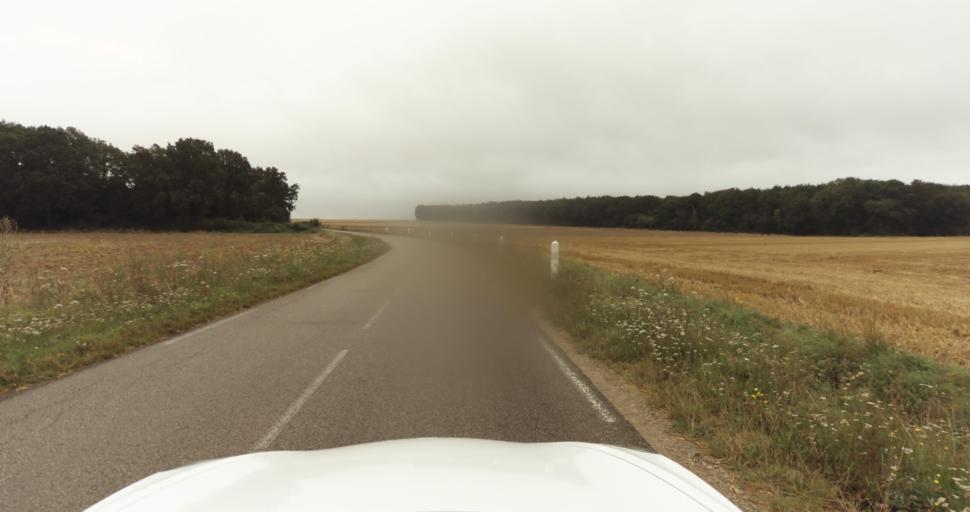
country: FR
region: Haute-Normandie
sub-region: Departement de l'Eure
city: Normanville
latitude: 49.0929
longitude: 1.1691
